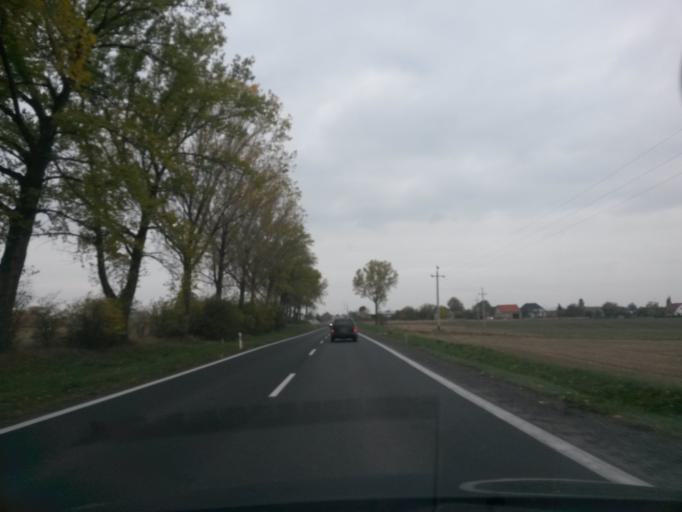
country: PL
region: Lower Silesian Voivodeship
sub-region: Powiat zabkowicki
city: Zabkowice Slaskie
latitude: 50.5506
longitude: 16.7986
